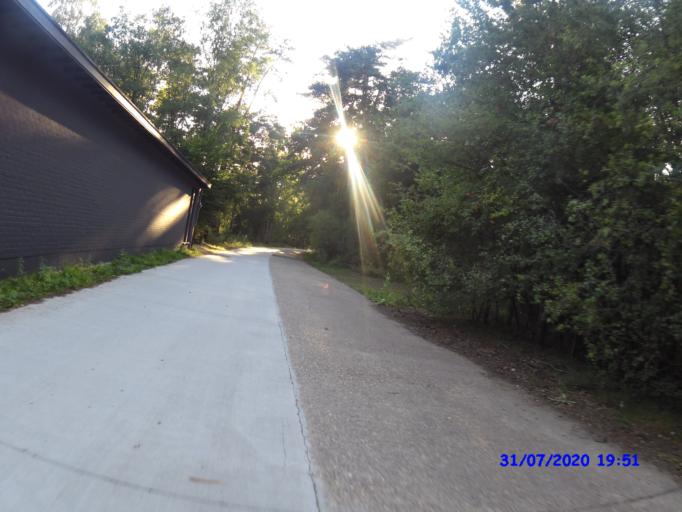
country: BE
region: Flanders
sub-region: Provincie Antwerpen
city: Kasterlee
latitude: 51.2398
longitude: 4.9319
